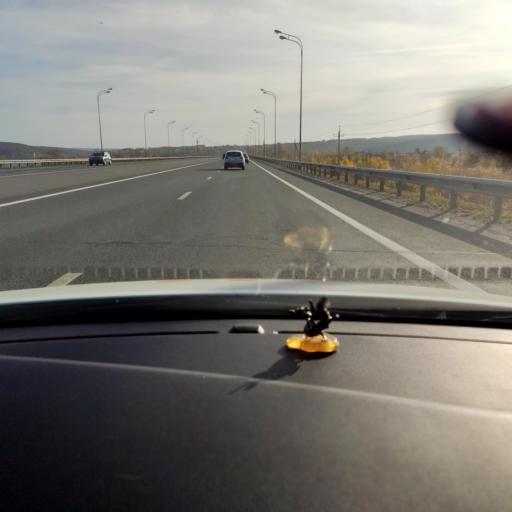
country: RU
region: Tatarstan
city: Osinovo
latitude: 55.8016
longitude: 48.8411
